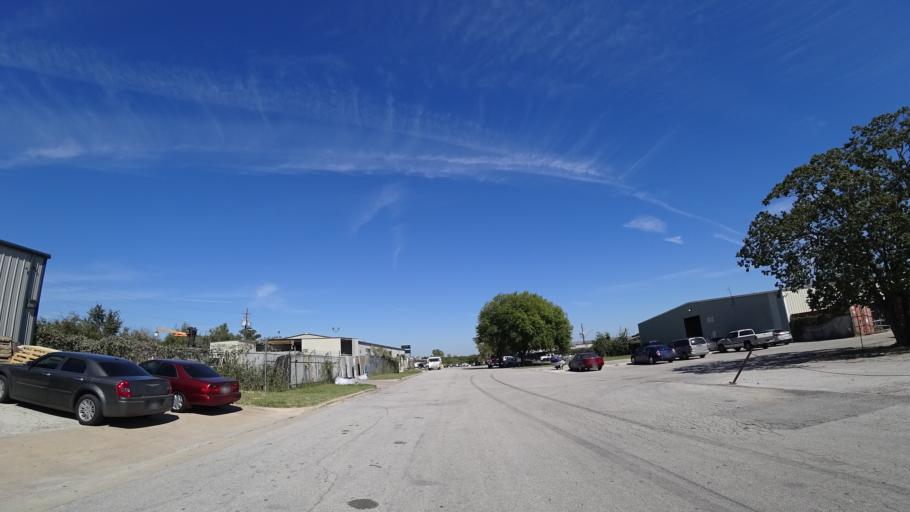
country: US
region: Texas
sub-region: Travis County
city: Austin
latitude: 30.1955
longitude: -97.7070
